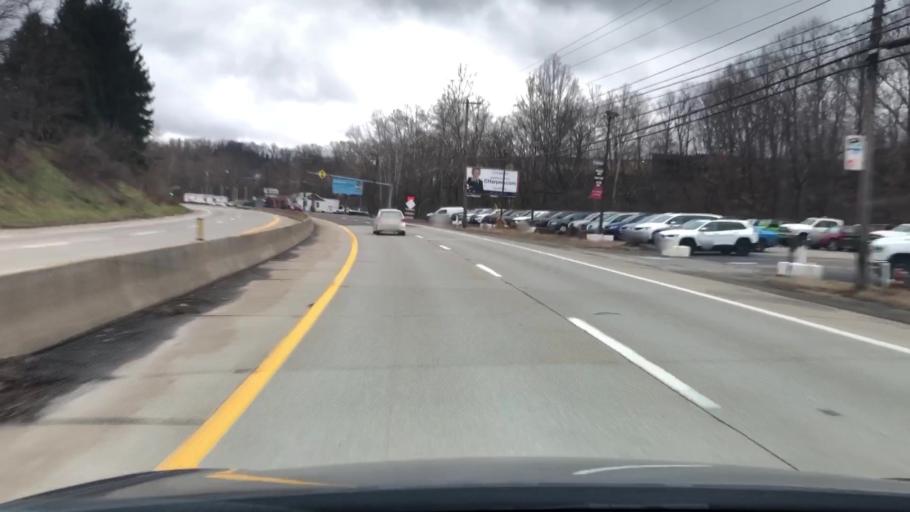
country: US
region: Pennsylvania
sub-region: Fayette County
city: Connellsville
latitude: 40.0464
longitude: -79.5713
